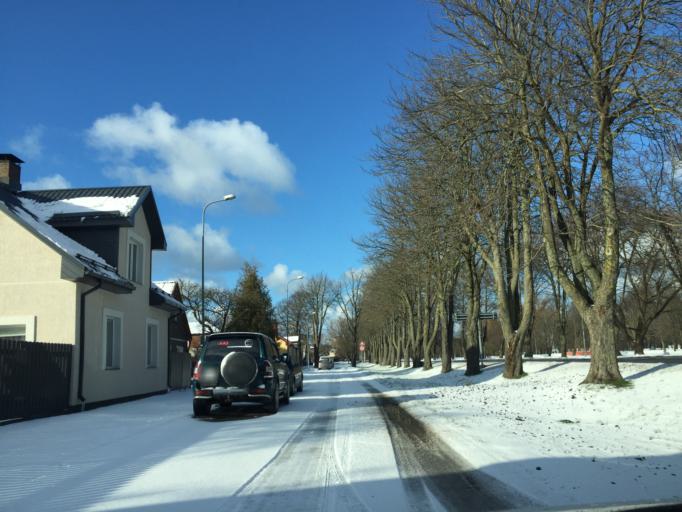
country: LV
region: Ventspils
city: Ventspils
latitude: 57.3823
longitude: 21.5662
